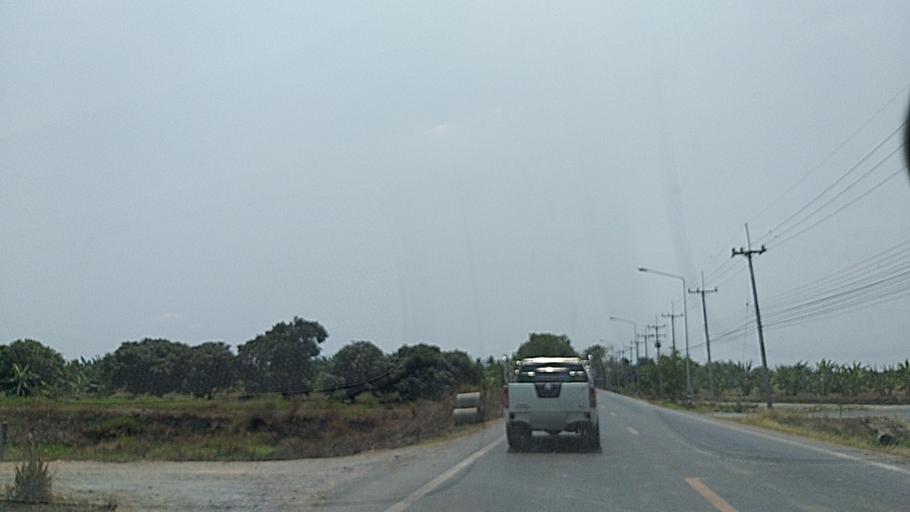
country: TH
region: Chachoengsao
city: Bang Nam Priao
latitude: 13.8556
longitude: 100.9655
